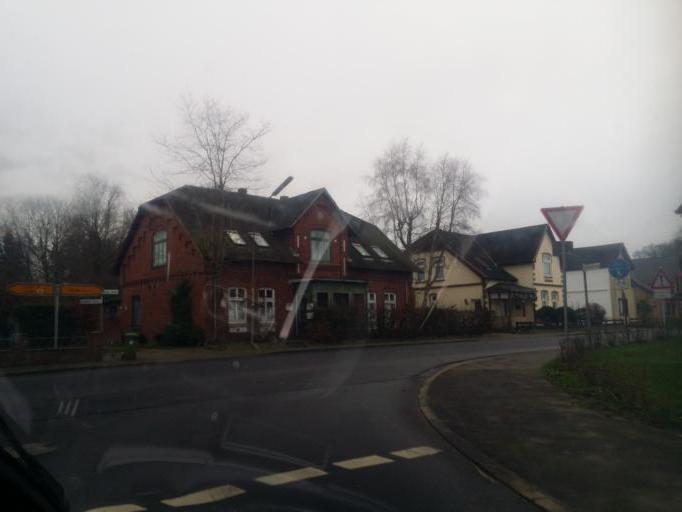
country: DE
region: Schleswig-Holstein
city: Norderheistedt
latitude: 54.2351
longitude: 9.1487
